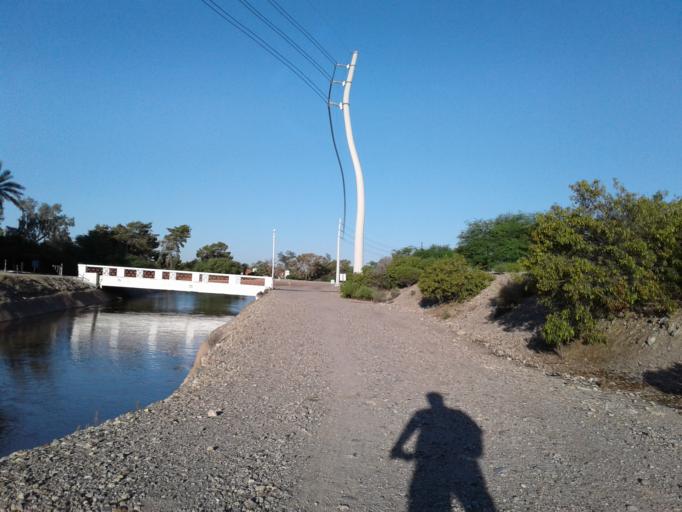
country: US
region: Arizona
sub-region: Maricopa County
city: Paradise Valley
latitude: 33.5239
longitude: -112.0259
